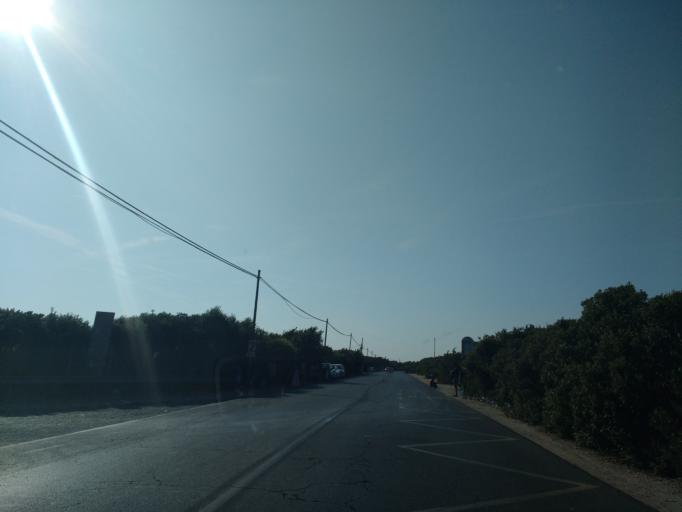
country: IT
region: Latium
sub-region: Citta metropolitana di Roma Capitale
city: Torvaianica
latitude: 41.6829
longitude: 12.3807
